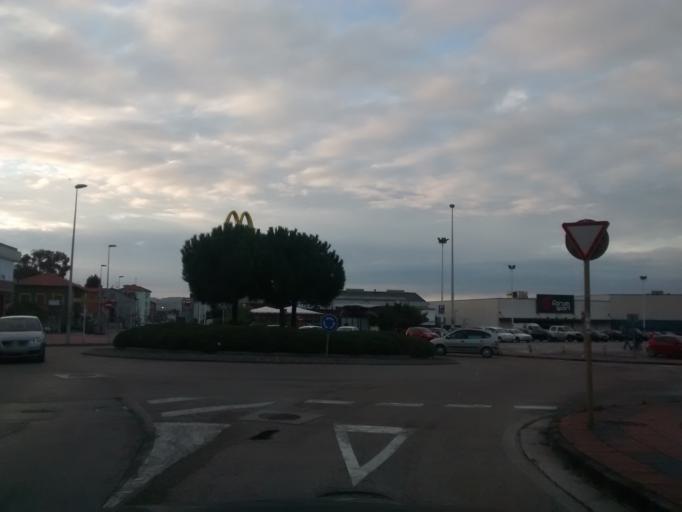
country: ES
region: Cantabria
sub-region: Provincia de Cantabria
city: Torrelavega
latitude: 43.3434
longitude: -4.0324
